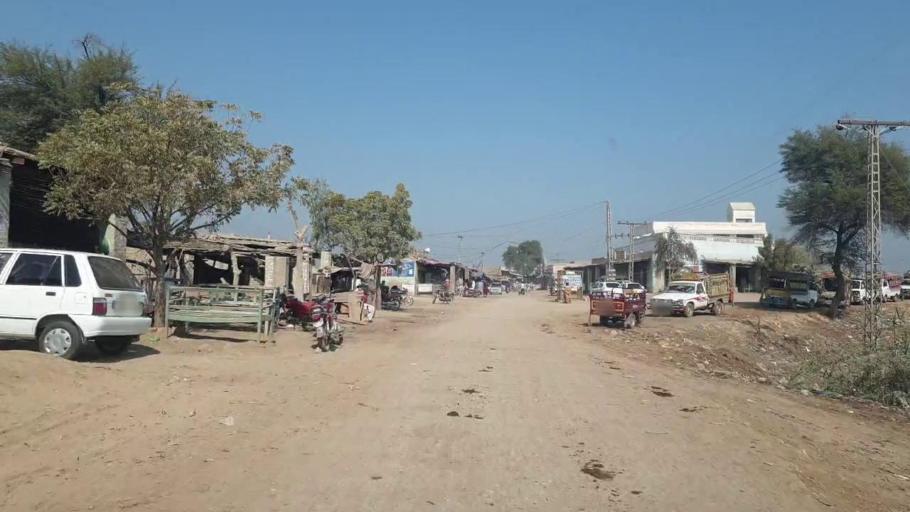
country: PK
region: Sindh
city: Sakrand
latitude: 26.0525
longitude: 68.4032
